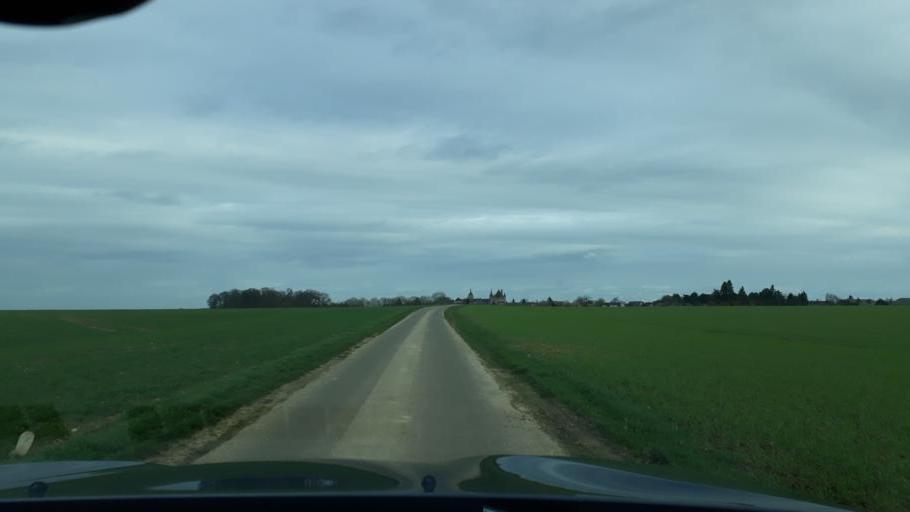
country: FR
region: Centre
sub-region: Departement du Loir-et-Cher
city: Mer
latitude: 47.7719
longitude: 1.4333
